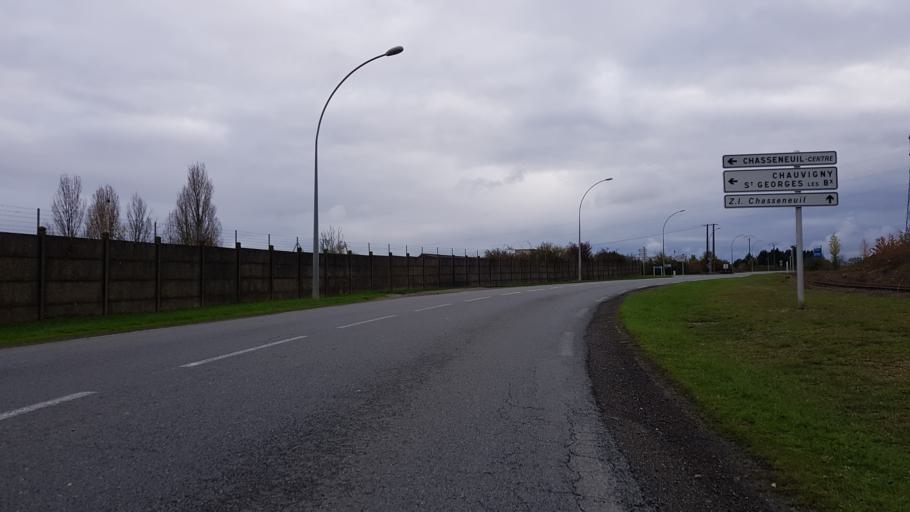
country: FR
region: Poitou-Charentes
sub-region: Departement de la Vienne
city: Chasseneuil-du-Poitou
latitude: 46.6645
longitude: 0.3764
